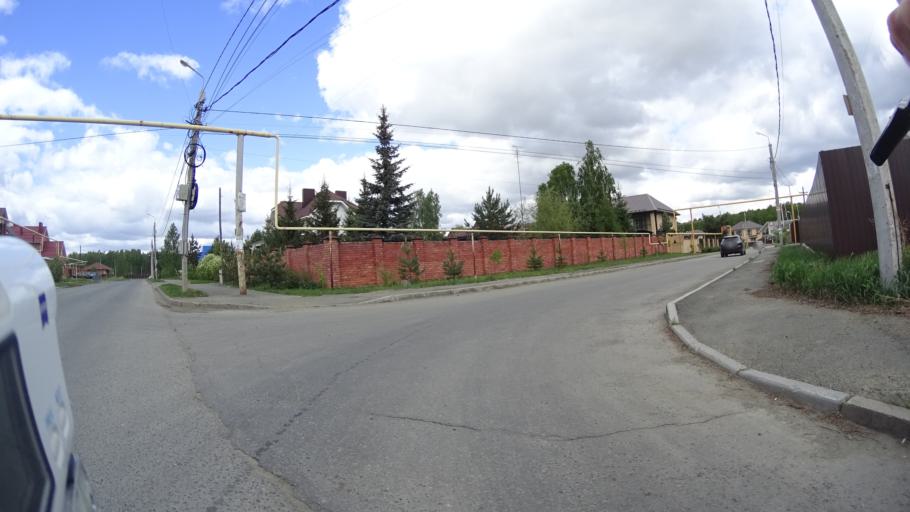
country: RU
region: Chelyabinsk
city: Sargazy
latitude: 55.1594
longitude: 61.2519
